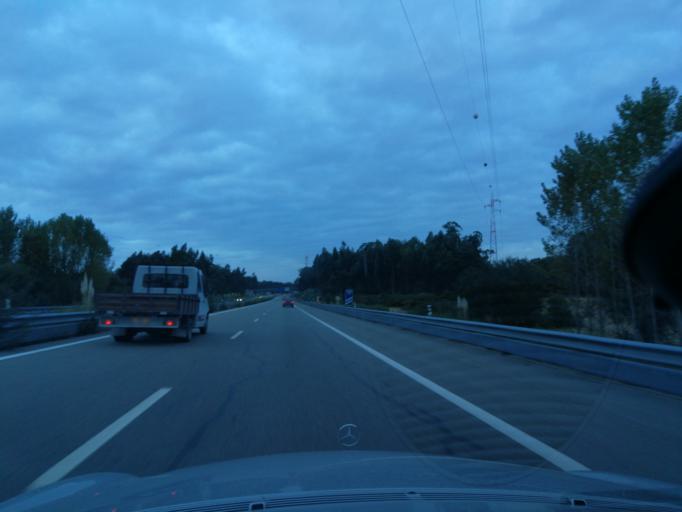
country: PT
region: Aveiro
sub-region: Estarreja
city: Beduido
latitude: 40.7774
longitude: -8.5613
